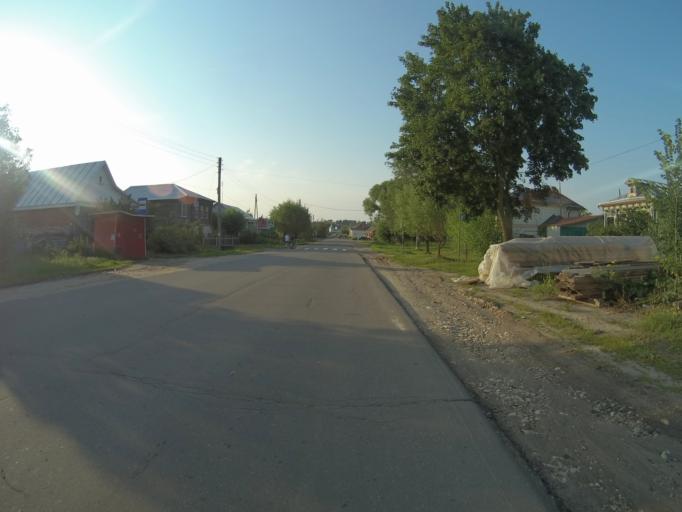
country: RU
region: Vladimir
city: Bogolyubovo
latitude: 56.2707
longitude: 40.4829
